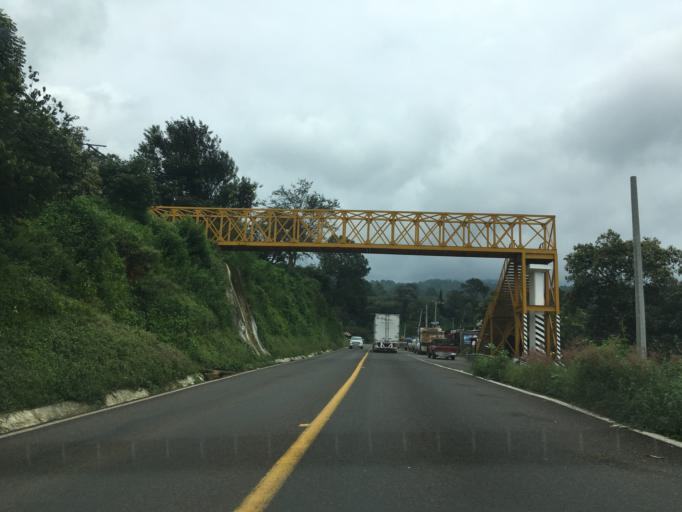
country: MX
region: Michoacan
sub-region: Uruapan
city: Toreo Bajo (El Toreo Bajo)
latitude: 19.4671
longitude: -101.9456
